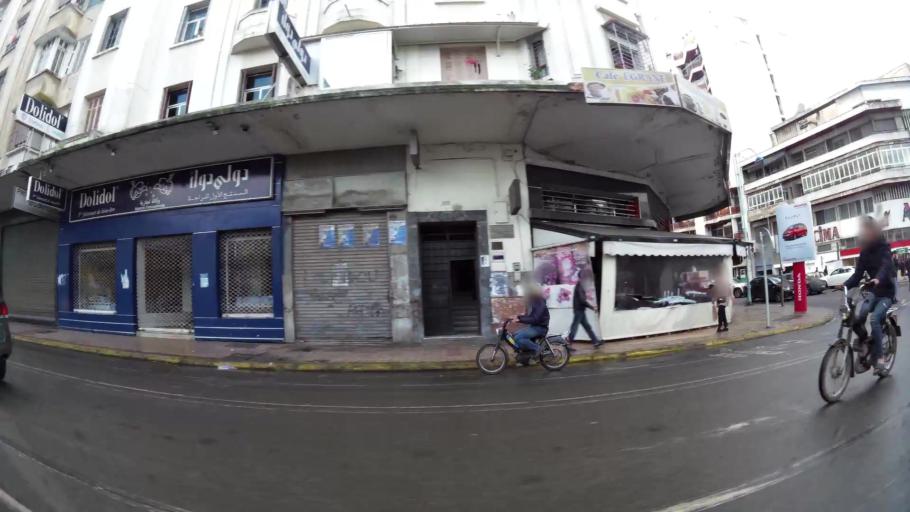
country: MA
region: Grand Casablanca
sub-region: Casablanca
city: Casablanca
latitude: 33.5881
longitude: -7.6121
